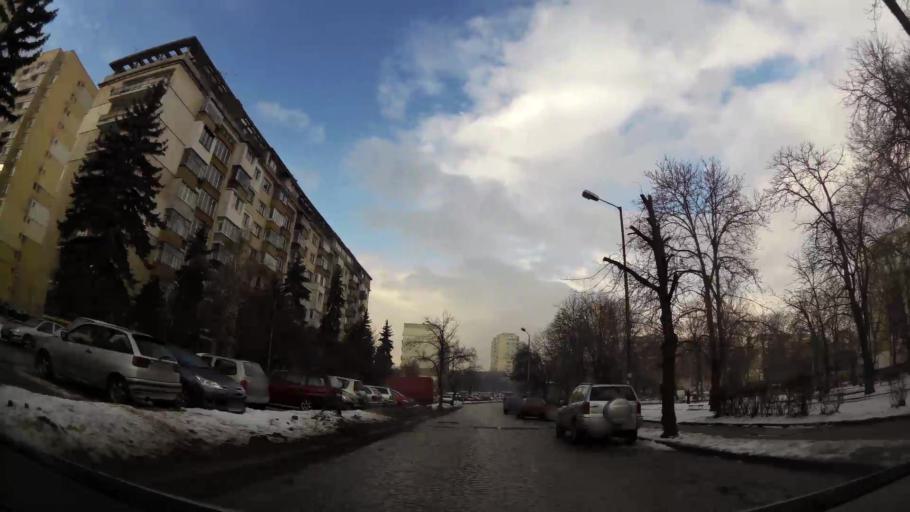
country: BG
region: Sofia-Capital
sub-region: Stolichna Obshtina
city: Sofia
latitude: 42.6961
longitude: 23.2822
